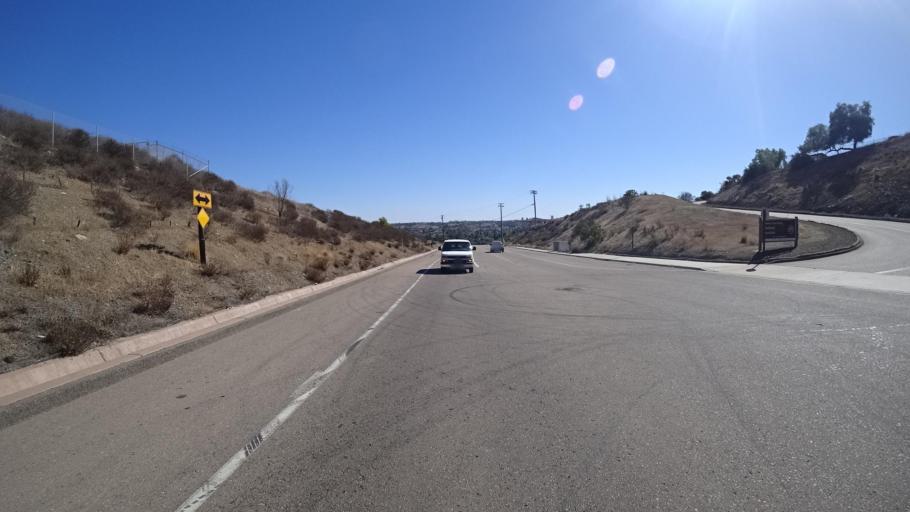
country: US
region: California
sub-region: San Diego County
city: La Presa
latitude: 32.6898
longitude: -117.0166
